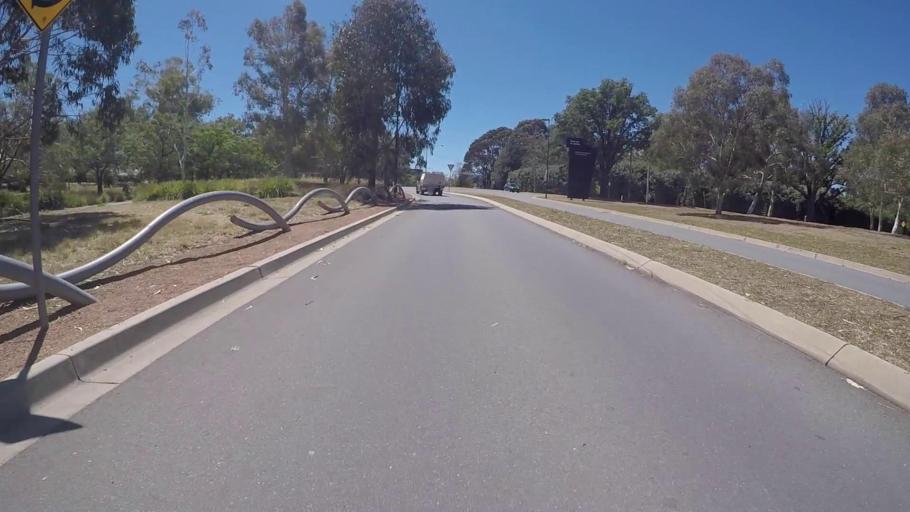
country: AU
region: Australian Capital Territory
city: Canberra
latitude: -35.2908
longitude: 149.1176
